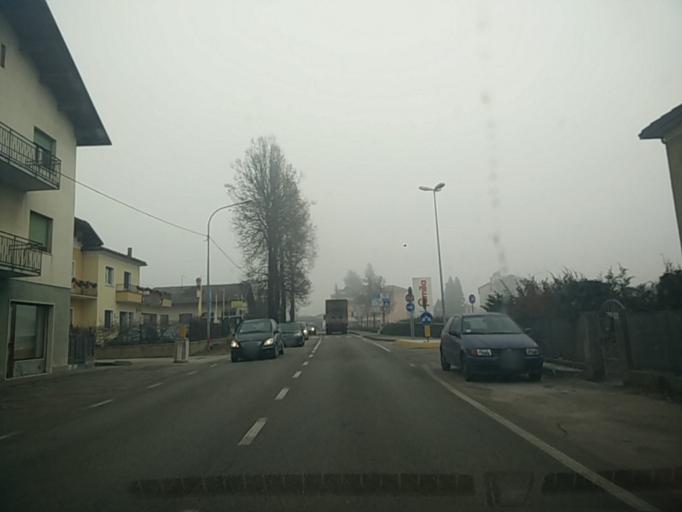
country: IT
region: Veneto
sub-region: Provincia di Belluno
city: Feltre
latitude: 46.0190
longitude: 11.8917
